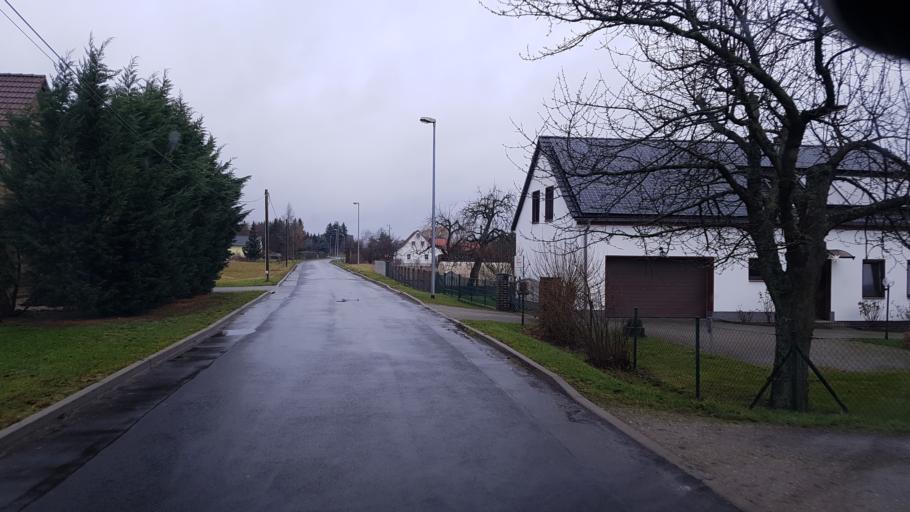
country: DE
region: Brandenburg
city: Altdobern
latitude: 51.6734
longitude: 13.9862
